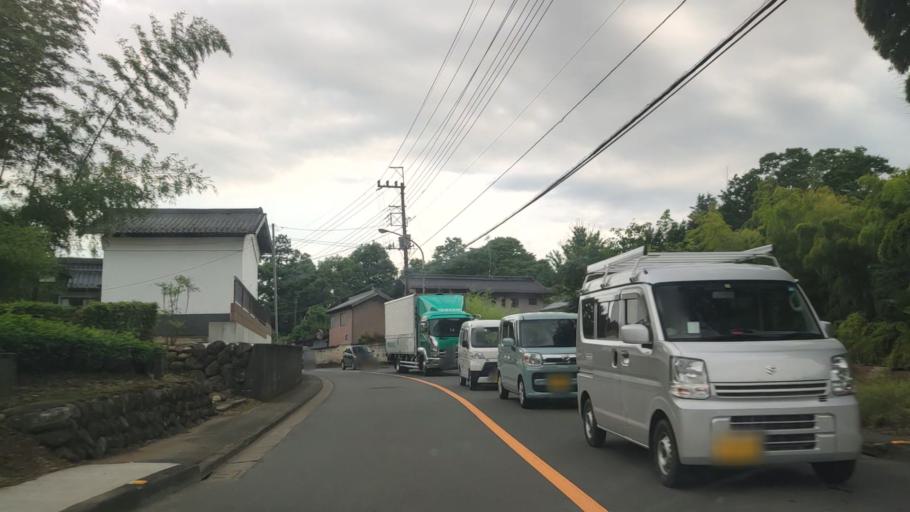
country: JP
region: Saitama
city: Hanno
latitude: 35.8318
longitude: 139.2963
